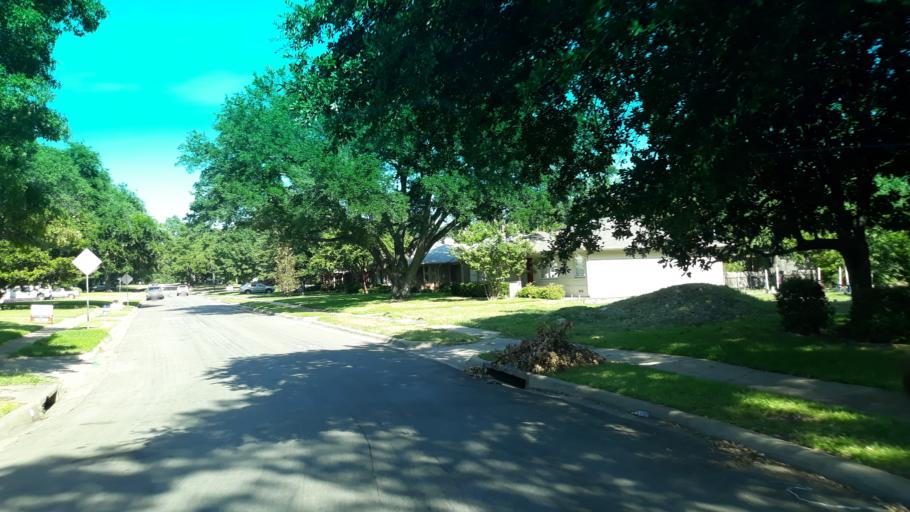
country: US
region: Texas
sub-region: Dallas County
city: Highland Park
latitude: 32.8266
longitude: -96.7597
